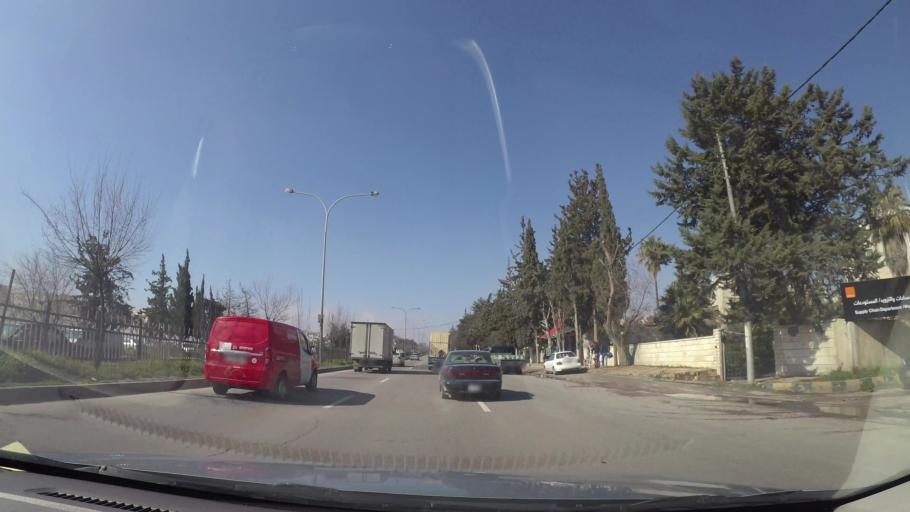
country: JO
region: Amman
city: Al Bunayyat ash Shamaliyah
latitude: 31.9035
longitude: 35.8774
